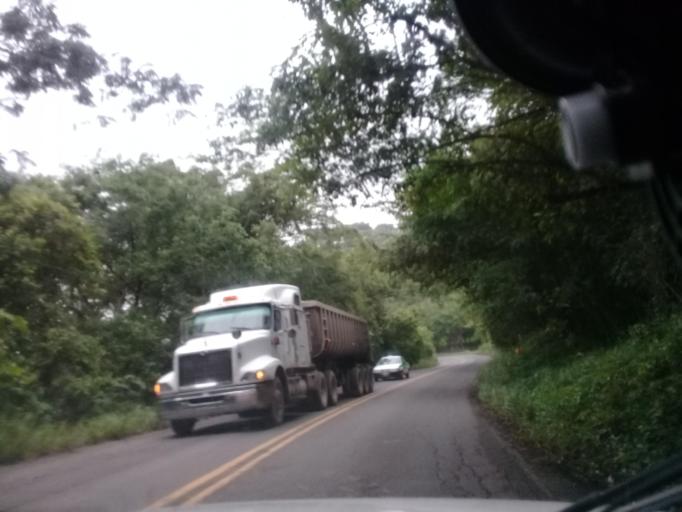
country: MX
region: Veracruz
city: Platon Sanchez
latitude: 21.2392
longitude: -98.3691
